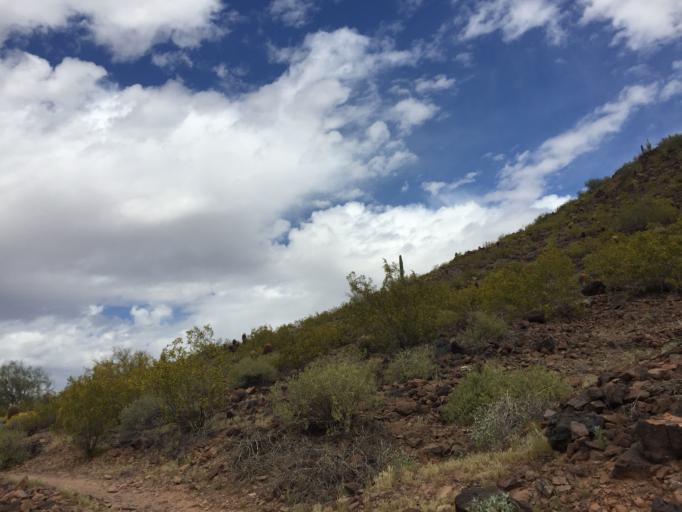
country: US
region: Arizona
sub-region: Maricopa County
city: Peoria
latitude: 33.6880
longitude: -112.1844
